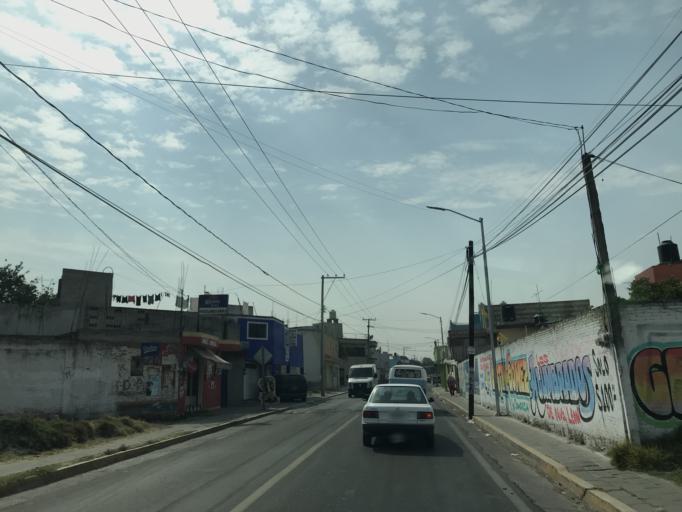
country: MX
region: Tlaxcala
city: Tenancingo
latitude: 19.1434
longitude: -98.1936
